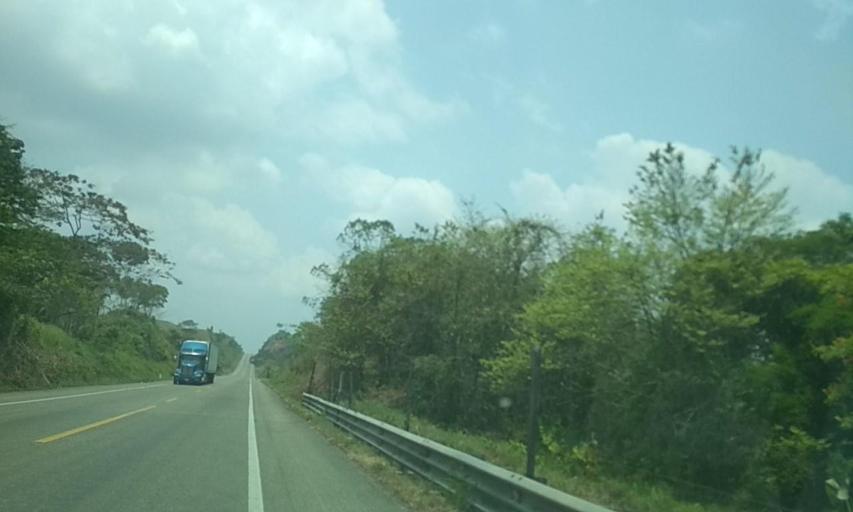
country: MX
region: Tabasco
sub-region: Huimanguillo
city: Francisco Rueda
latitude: 17.6529
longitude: -93.8411
